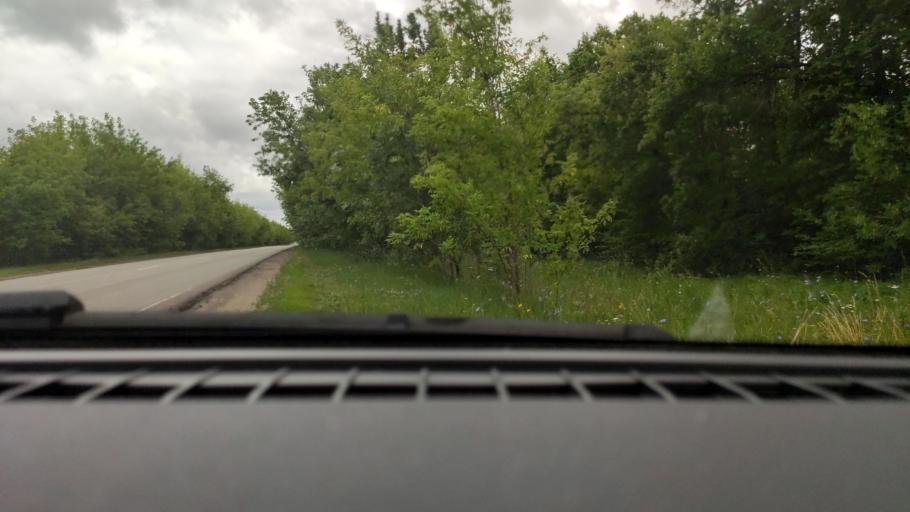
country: RU
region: Voronezj
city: Zemlyansk
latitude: 51.8736
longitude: 38.7752
